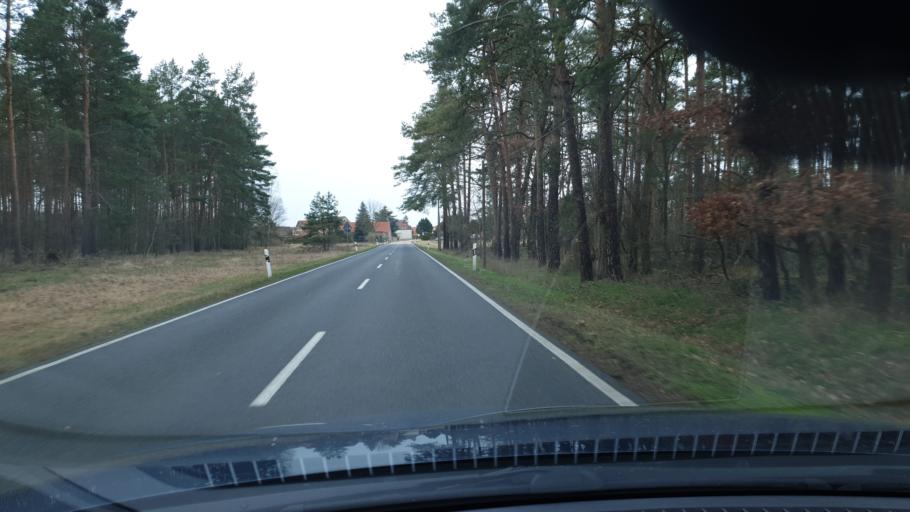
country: DE
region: Saxony-Anhalt
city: Radis
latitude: 51.7791
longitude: 12.4883
